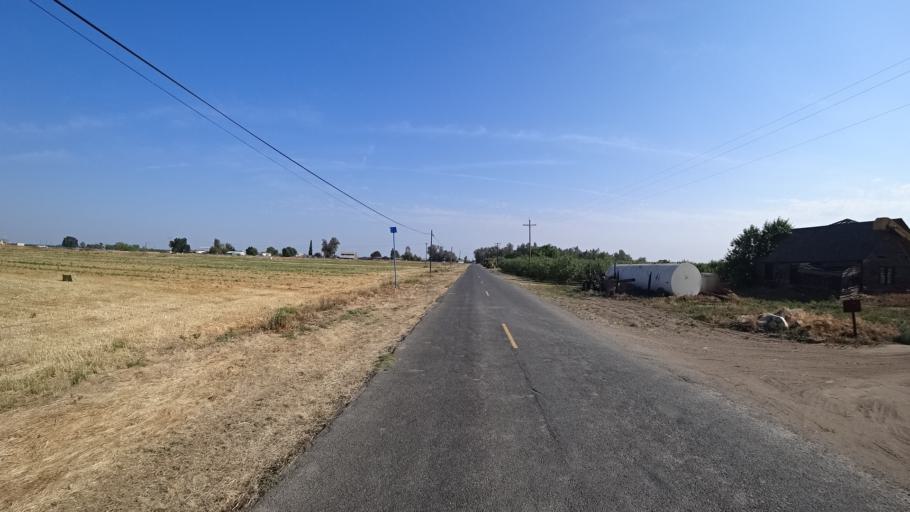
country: US
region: California
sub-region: Fresno County
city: Riverdale
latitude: 36.3767
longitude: -119.8163
